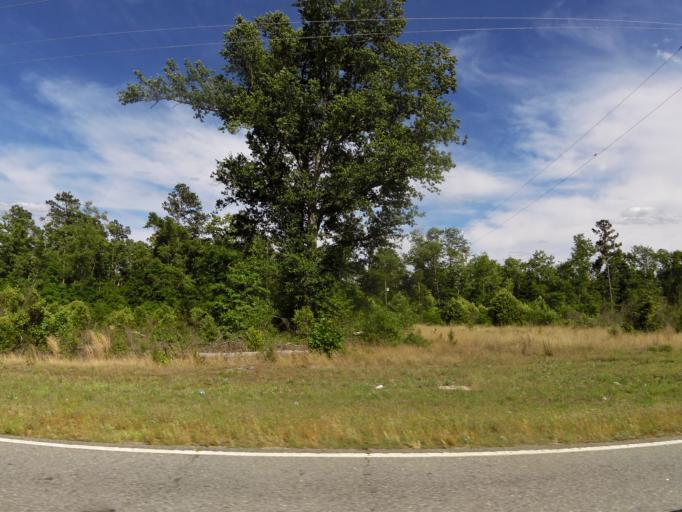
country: US
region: South Carolina
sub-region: Bamberg County
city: Denmark
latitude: 33.2037
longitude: -81.1765
